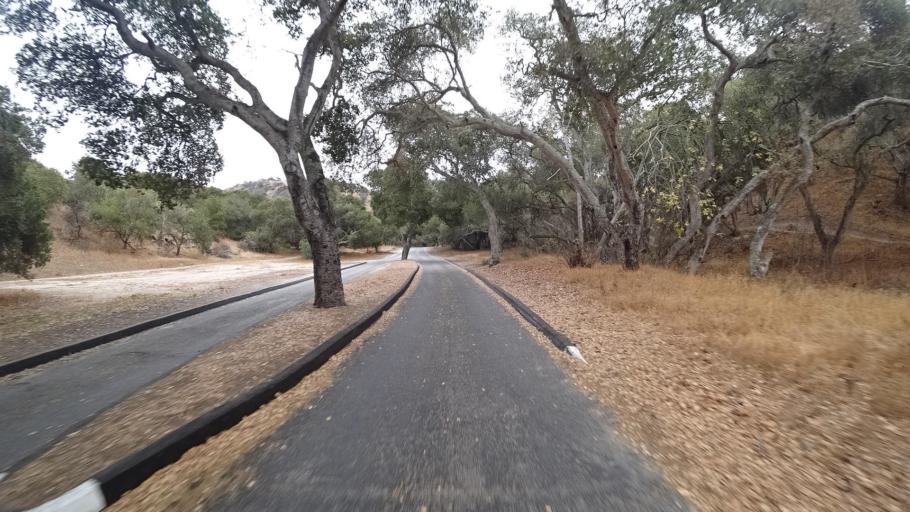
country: US
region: California
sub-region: Monterey County
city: Salinas
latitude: 36.5927
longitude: -121.6915
